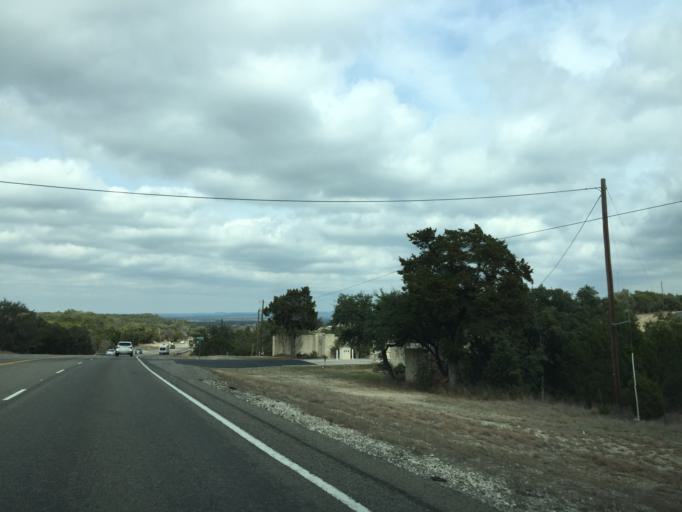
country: US
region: Texas
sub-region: Travis County
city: Briarcliff
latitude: 30.4429
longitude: -98.1472
